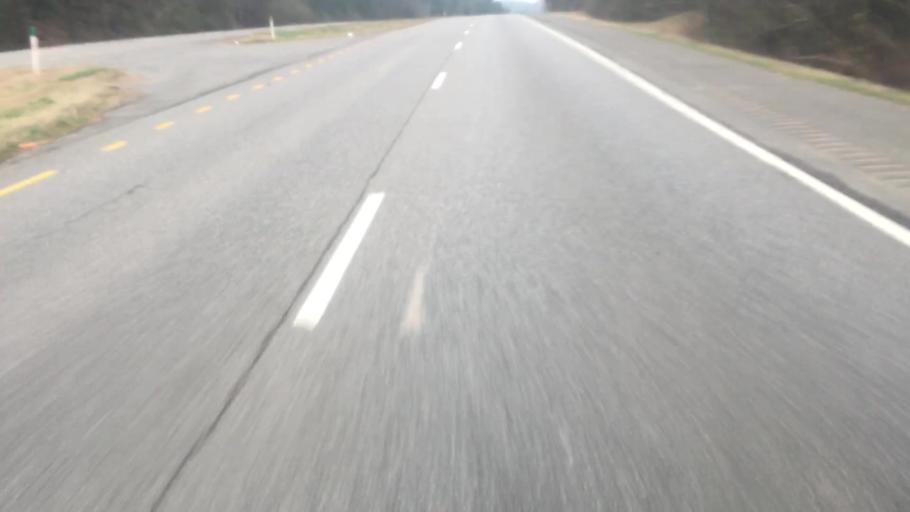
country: US
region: Alabama
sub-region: Jefferson County
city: Graysville
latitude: 33.6783
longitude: -86.9727
